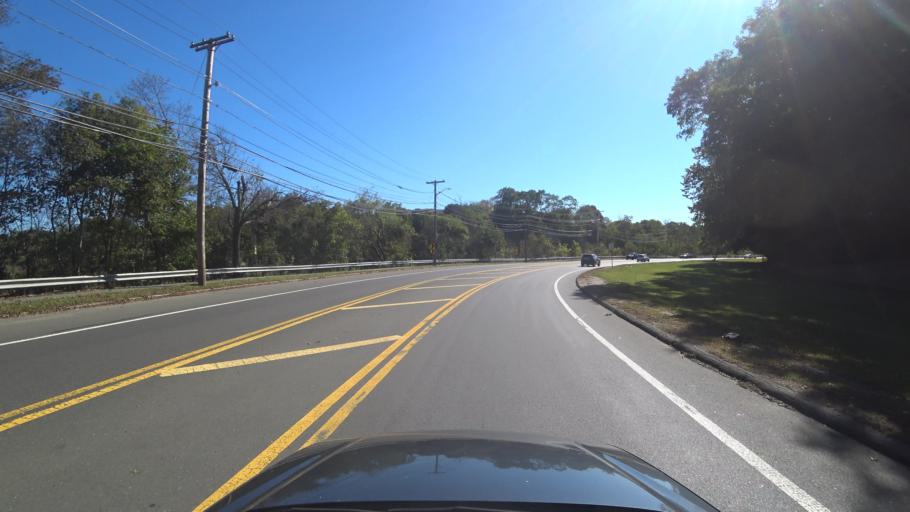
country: US
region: Massachusetts
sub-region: Essex County
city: Salem
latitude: 42.4933
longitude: -70.8926
